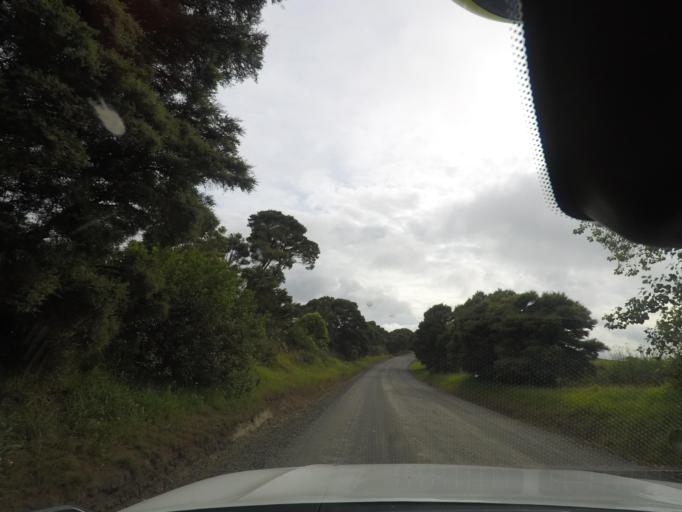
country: NZ
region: Auckland
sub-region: Auckland
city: Parakai
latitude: -36.4855
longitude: 174.2485
